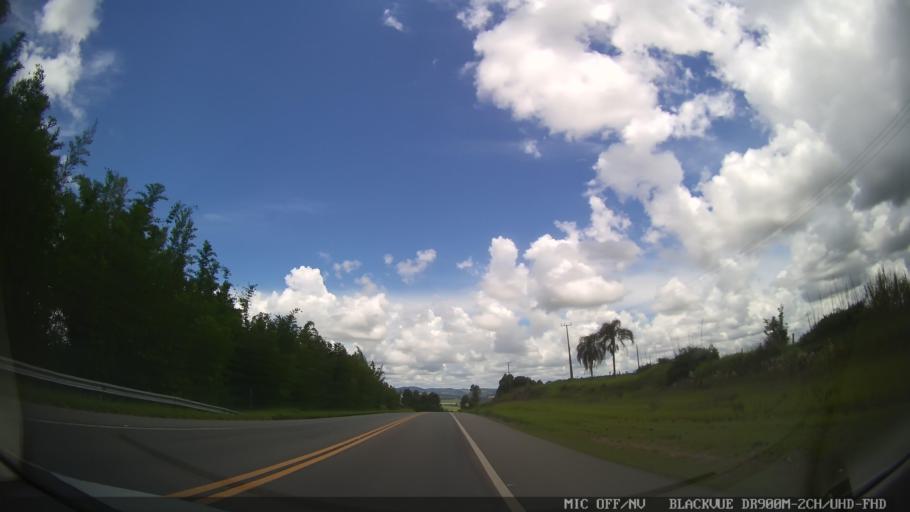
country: BR
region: Sao Paulo
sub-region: Braganca Paulista
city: Braganca Paulista
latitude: -22.8522
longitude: -46.6369
